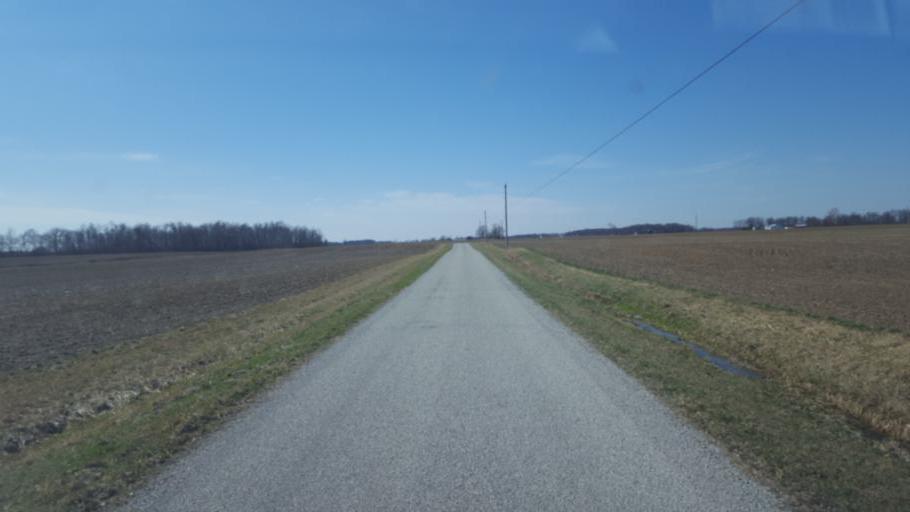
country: US
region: Ohio
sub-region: Union County
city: Richwood
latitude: 40.5117
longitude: -83.3560
